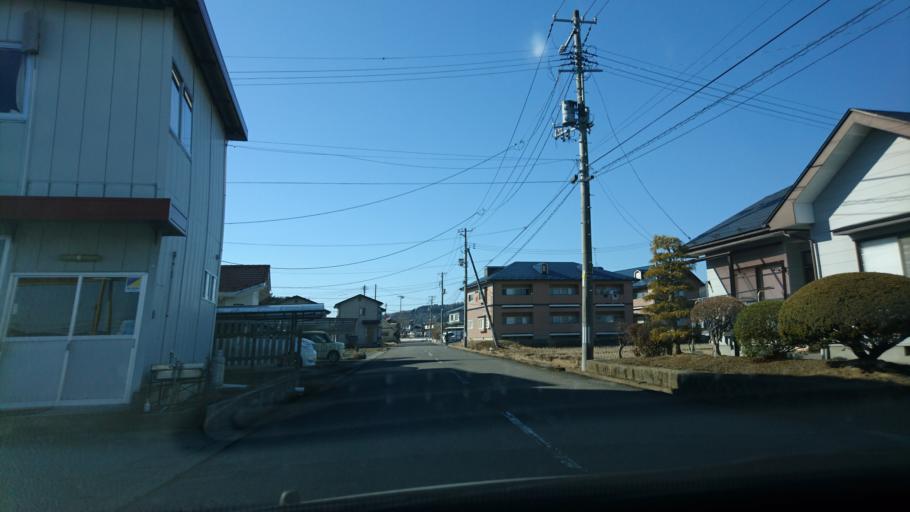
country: JP
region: Iwate
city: Ichinoseki
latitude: 38.9351
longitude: 141.1075
